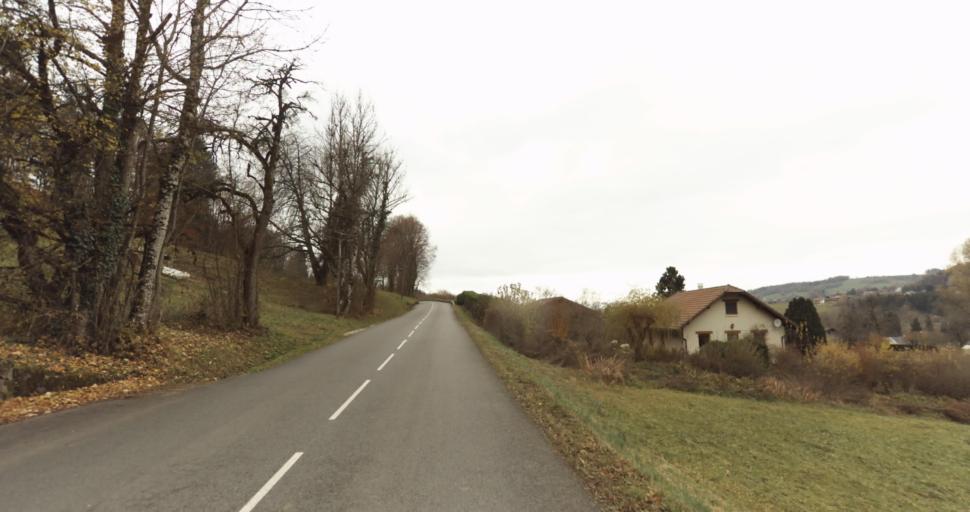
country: FR
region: Rhone-Alpes
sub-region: Departement de la Haute-Savoie
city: Thorens-Glieres
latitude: 45.9890
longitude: 6.2474
